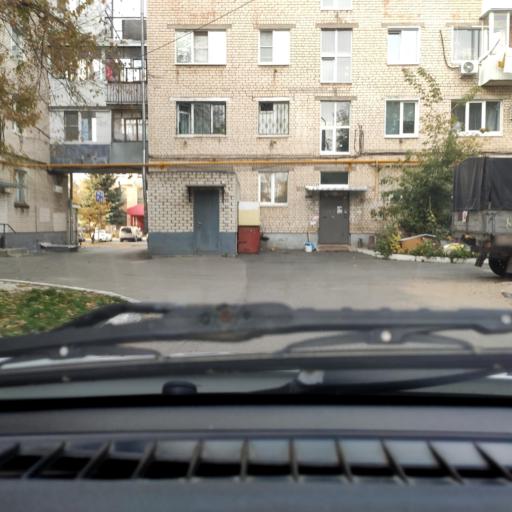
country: RU
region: Samara
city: Tol'yatti
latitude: 53.5067
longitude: 49.4061
